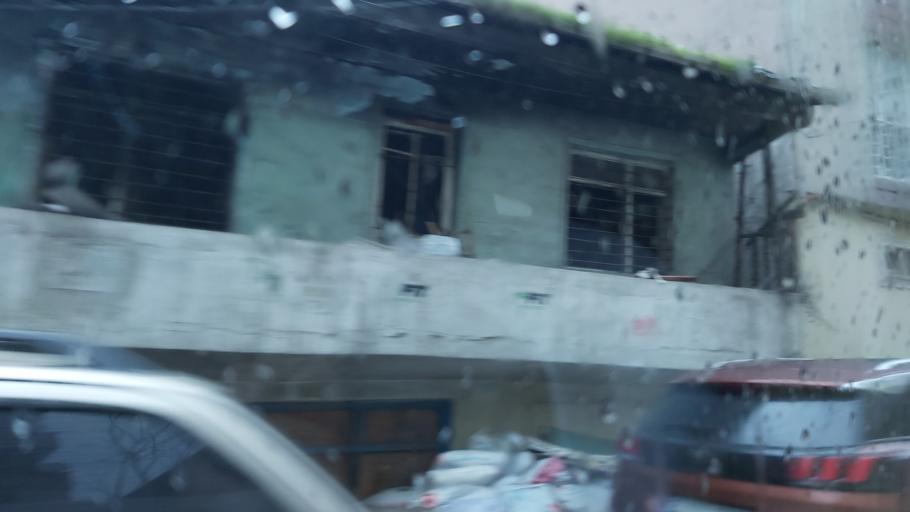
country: TR
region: Istanbul
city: Sisli
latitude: 41.0857
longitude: 28.9842
